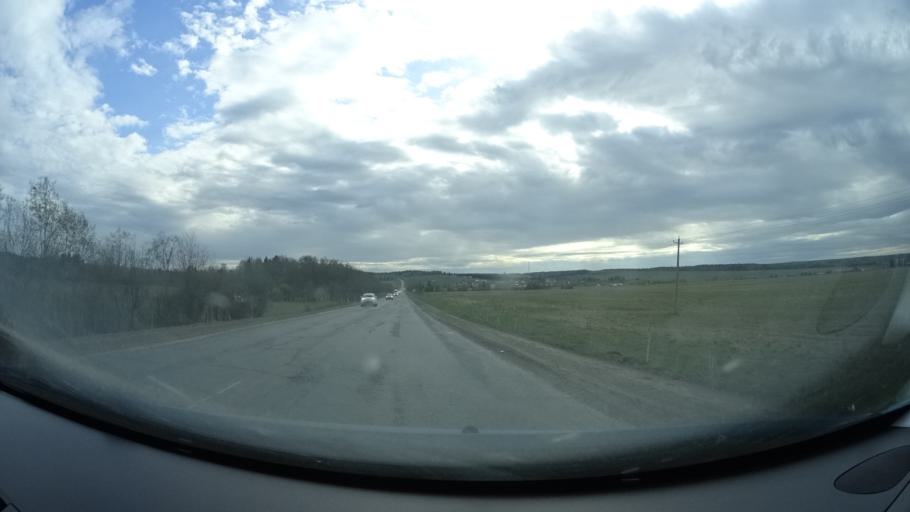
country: RU
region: Perm
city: Kultayevo
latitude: 57.8575
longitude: 55.8631
